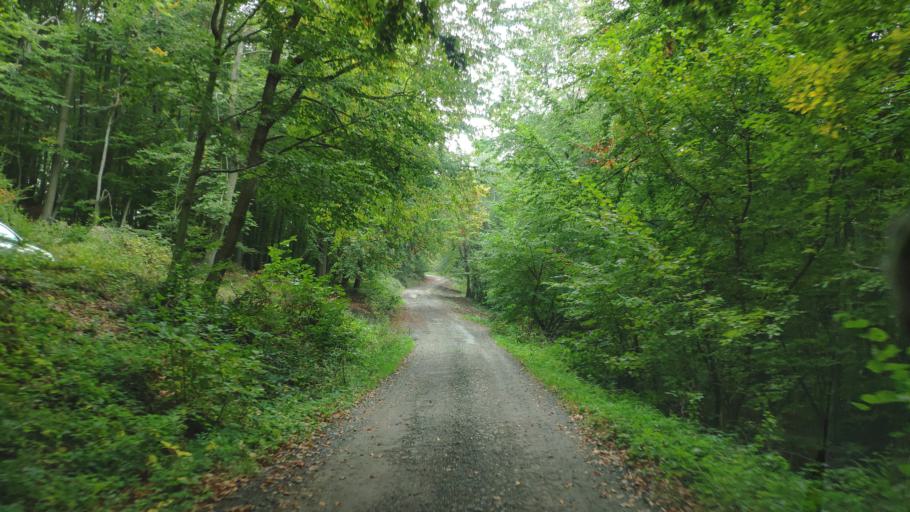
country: SK
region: Presovsky
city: Giraltovce
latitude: 48.9095
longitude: 21.4626
